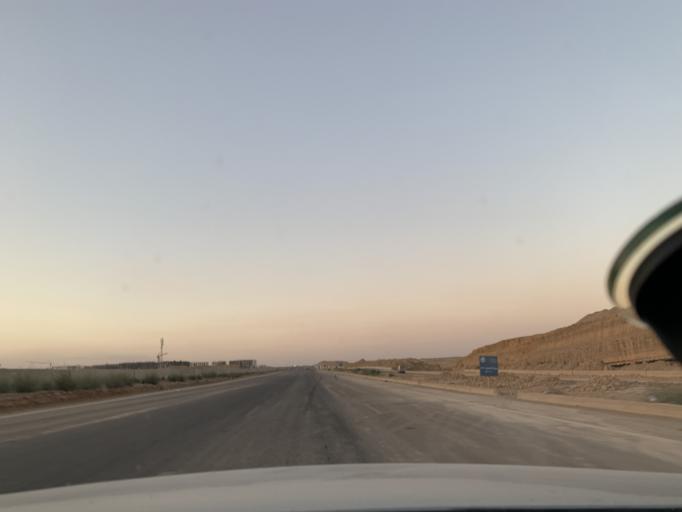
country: EG
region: Muhafazat al Qahirah
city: Halwan
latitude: 29.9591
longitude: 31.5445
